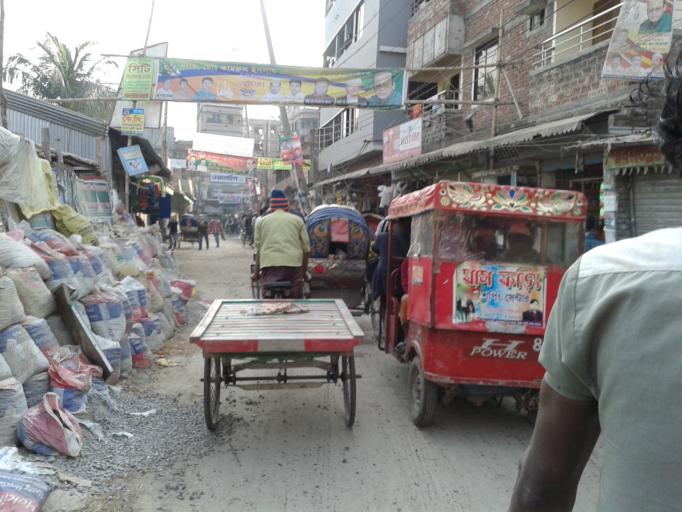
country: BD
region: Dhaka
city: Azimpur
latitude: 23.7192
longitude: 90.3730
